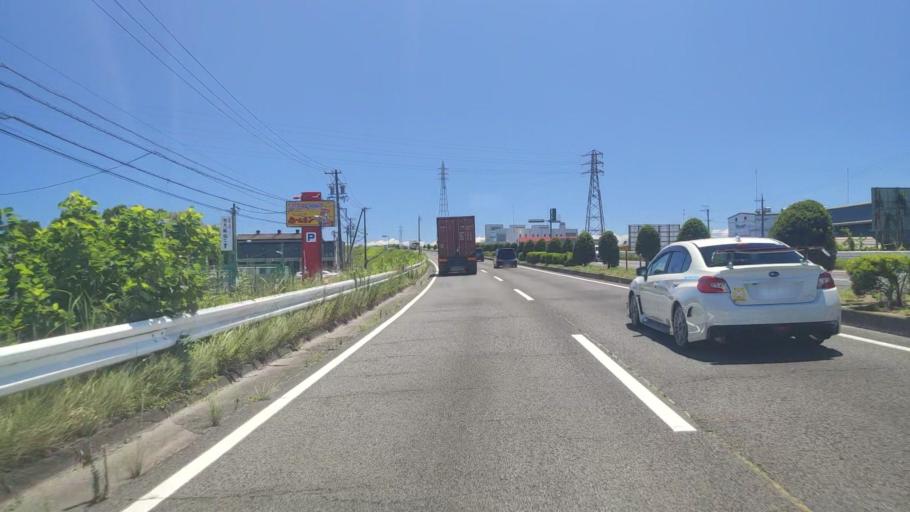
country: JP
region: Mie
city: Suzuka
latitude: 34.9123
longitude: 136.6054
